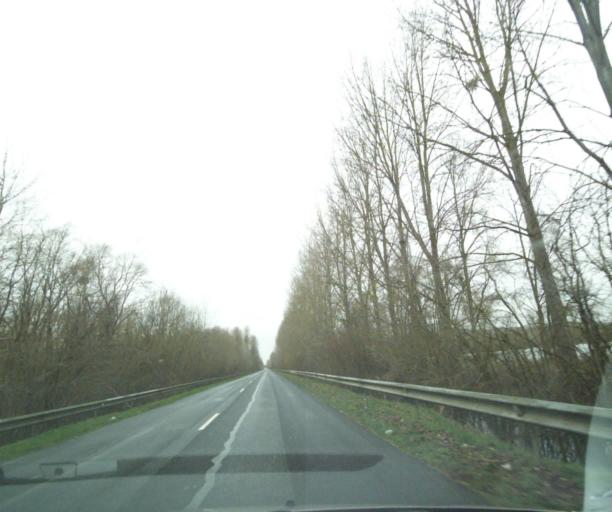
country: FR
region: Picardie
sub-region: Departement de l'Oise
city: Carlepont
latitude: 49.5577
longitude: 3.0405
